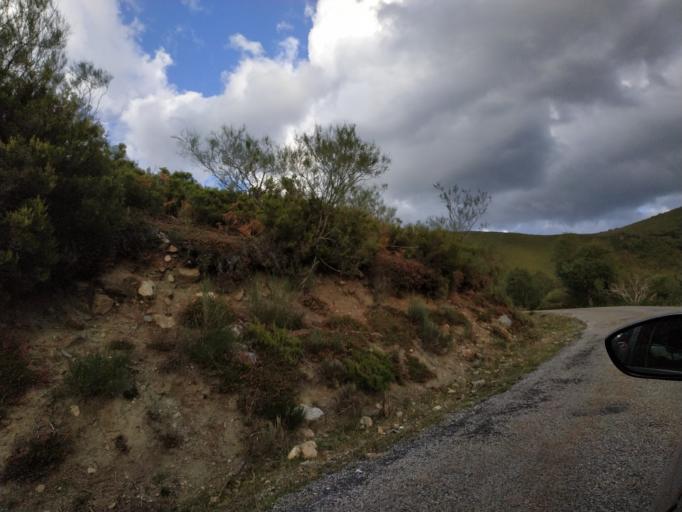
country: ES
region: Castille and Leon
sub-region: Provincia de Leon
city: Candin
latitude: 42.8682
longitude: -6.8406
